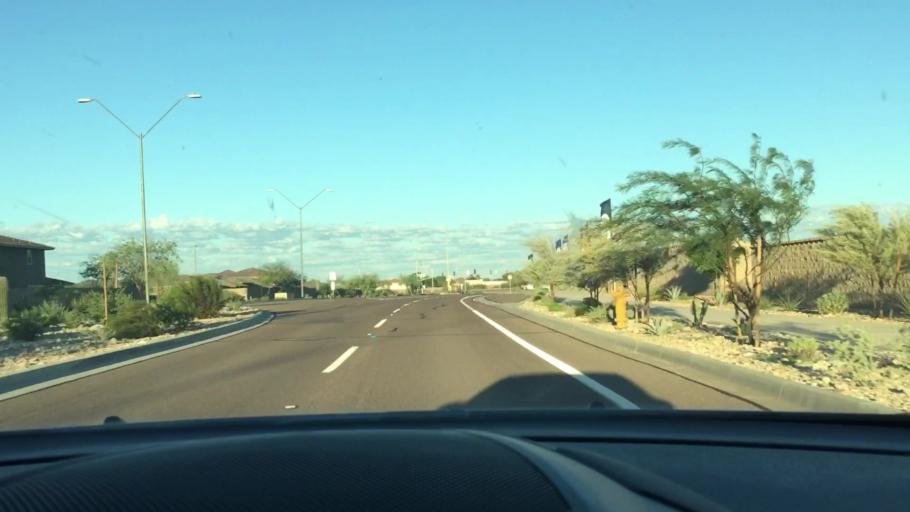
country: US
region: Arizona
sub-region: Maricopa County
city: Sun City West
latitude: 33.7377
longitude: -112.2591
